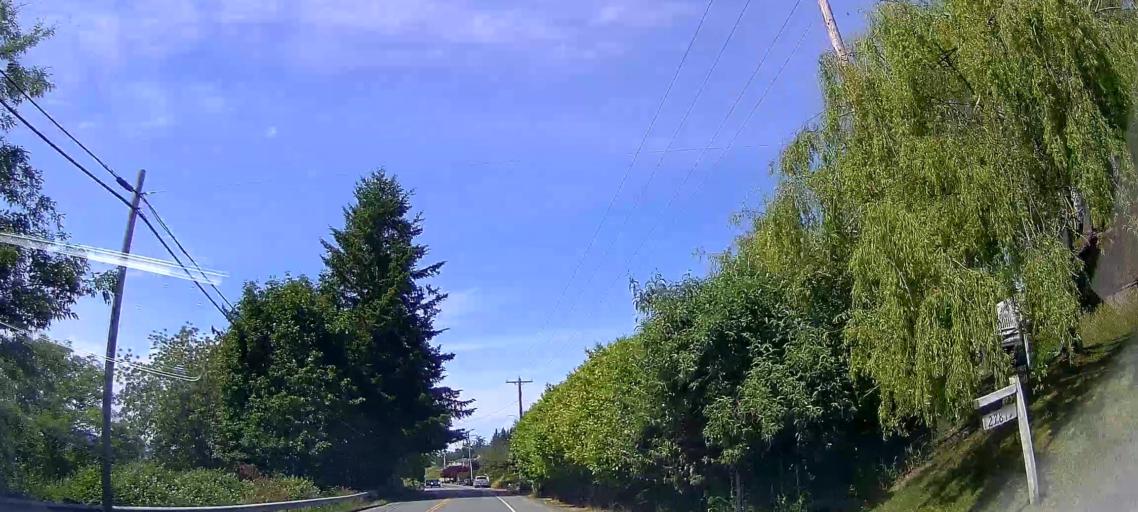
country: US
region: Washington
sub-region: Snohomish County
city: Stanwood
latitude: 48.2489
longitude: -122.3504
